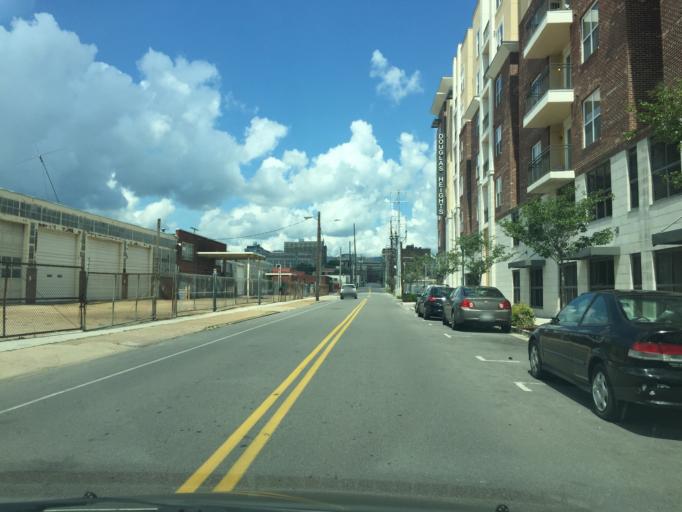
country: US
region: Tennessee
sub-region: Hamilton County
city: Chattanooga
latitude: 35.0424
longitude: -85.3026
